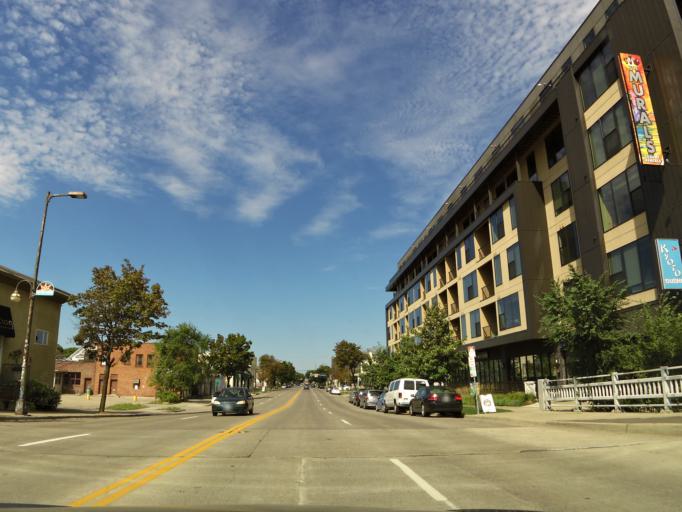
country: US
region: Minnesota
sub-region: Hennepin County
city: Minneapolis
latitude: 44.9502
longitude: -93.2882
